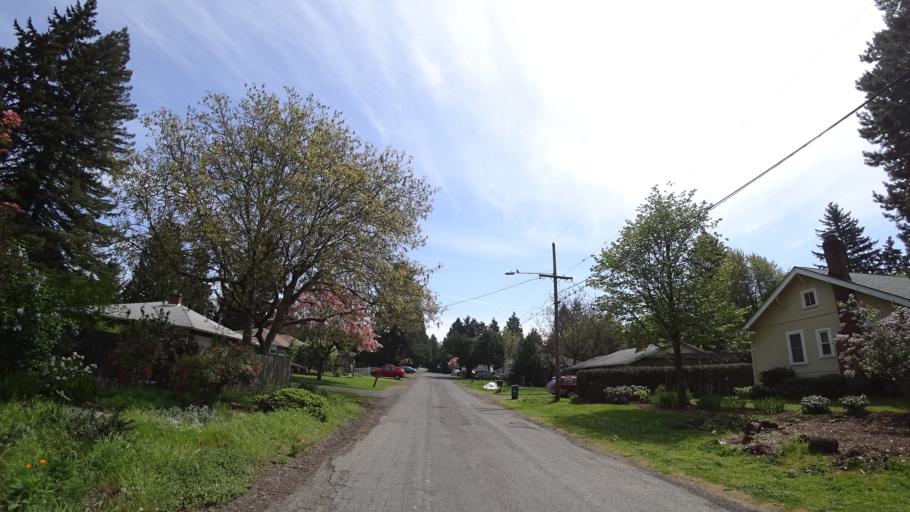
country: US
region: Oregon
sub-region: Clackamas County
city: Milwaukie
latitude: 45.4459
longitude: -122.6118
